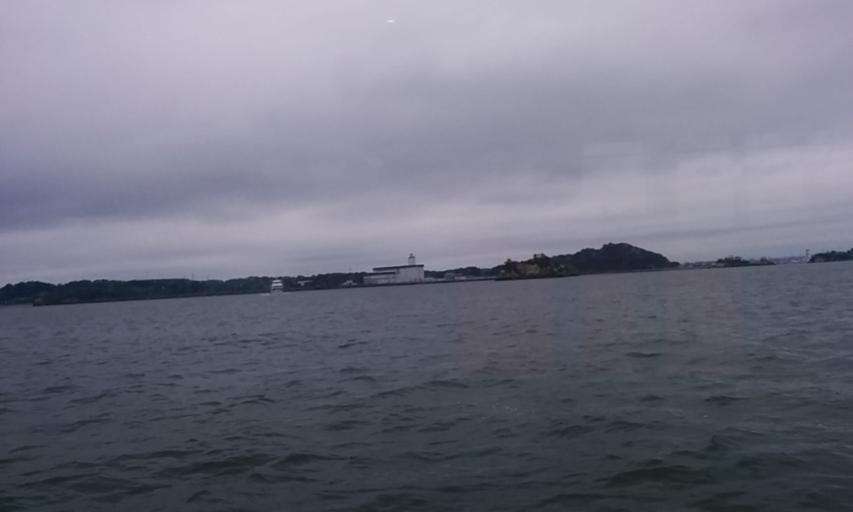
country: JP
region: Miyagi
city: Matsushima
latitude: 38.3265
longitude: 141.0864
